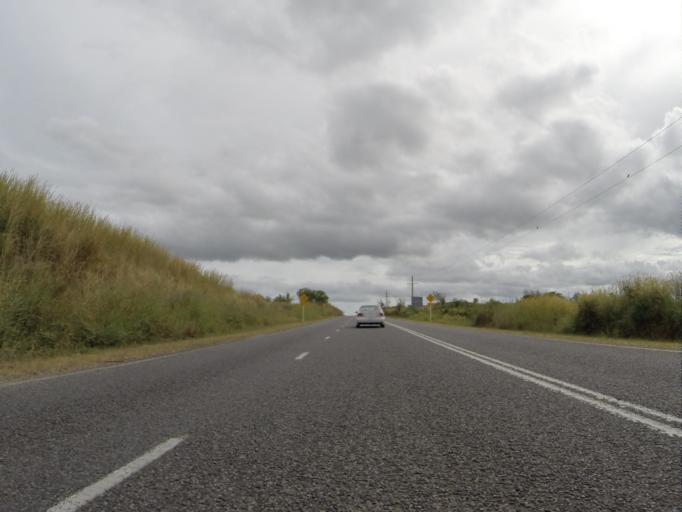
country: FJ
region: Western
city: Nadi
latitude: -18.0343
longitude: 177.3343
